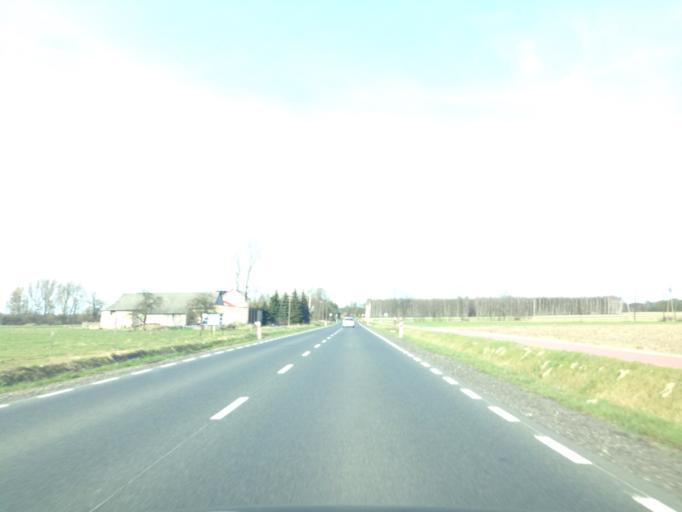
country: PL
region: Lodz Voivodeship
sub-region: Powiat poddebicki
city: Wartkowice
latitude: 51.9380
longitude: 18.9932
